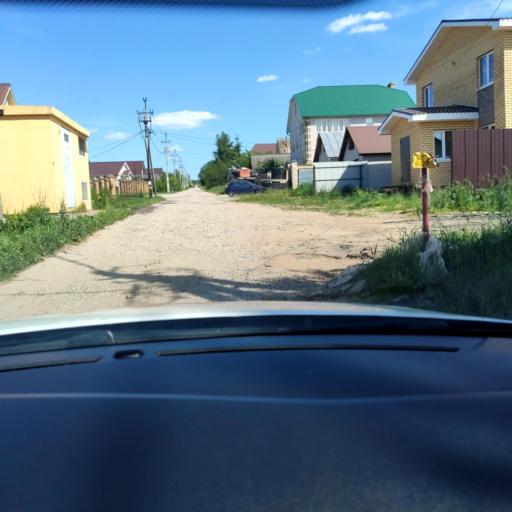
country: RU
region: Tatarstan
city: Stolbishchi
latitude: 55.7773
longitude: 49.2597
